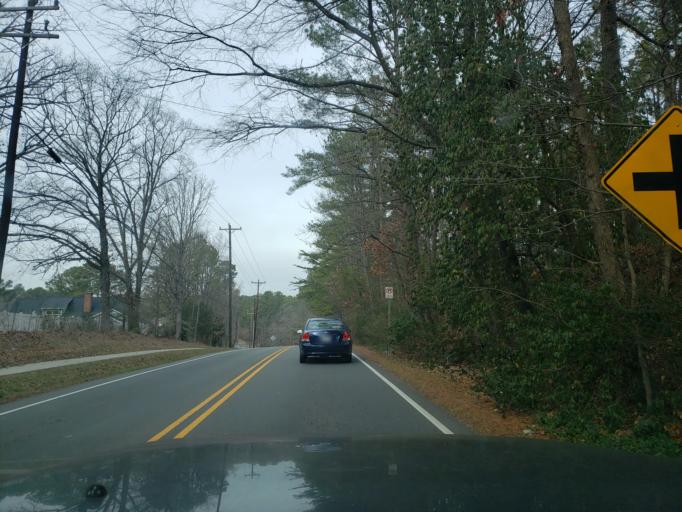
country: US
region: North Carolina
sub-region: Durham County
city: Durham
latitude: 35.9316
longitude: -78.9604
